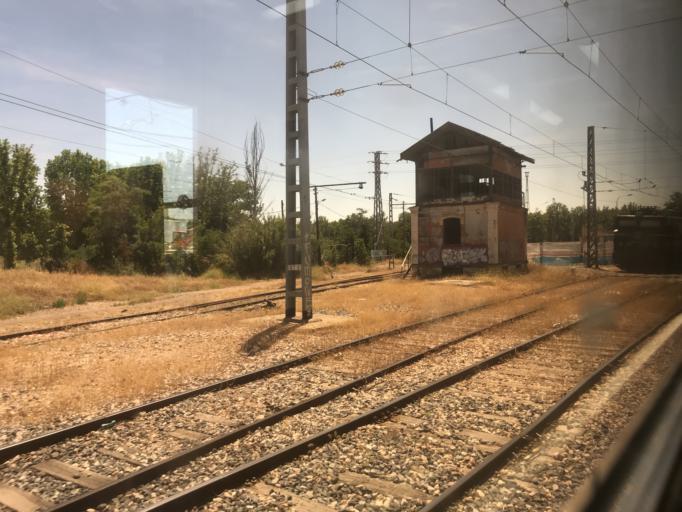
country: ES
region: Madrid
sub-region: Provincia de Madrid
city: Aranjuez
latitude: 40.0369
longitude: -3.6186
